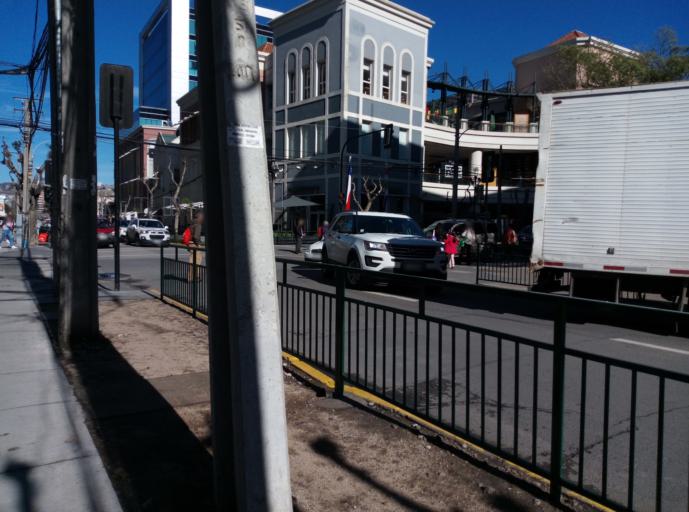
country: CL
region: Valparaiso
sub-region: Provincia de Valparaiso
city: Vina del Mar
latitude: -33.0093
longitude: -71.5462
